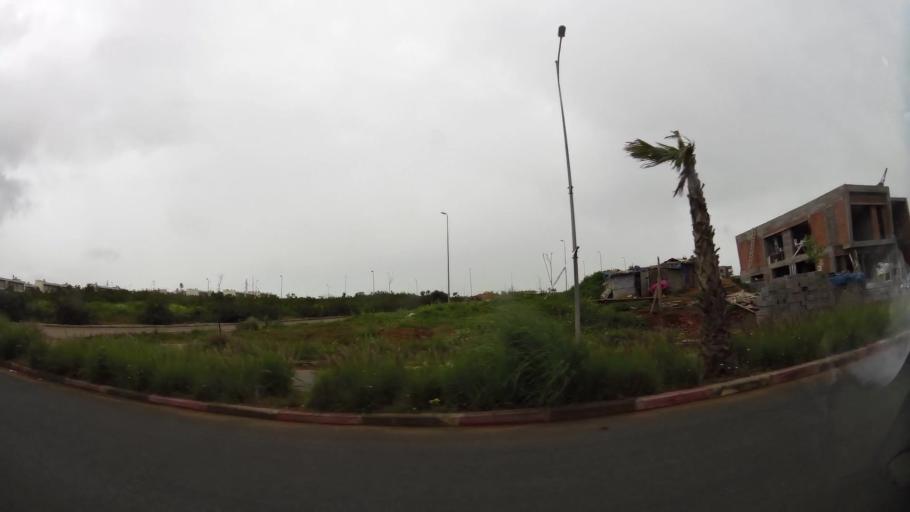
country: MA
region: Grand Casablanca
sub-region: Casablanca
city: Casablanca
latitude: 33.5241
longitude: -7.6225
